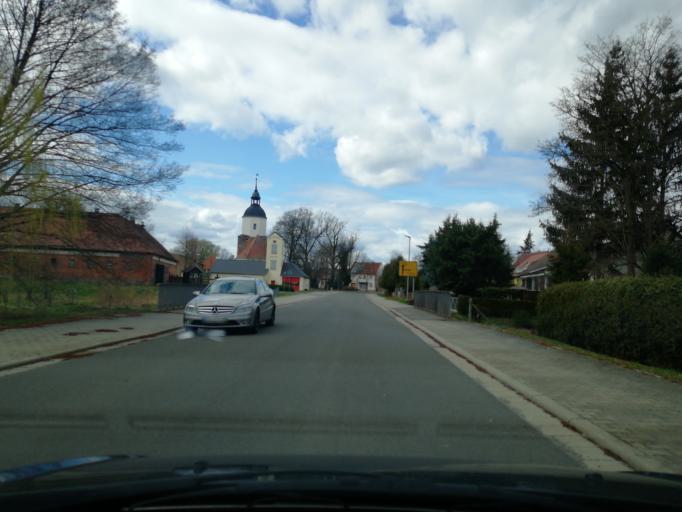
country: DE
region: Brandenburg
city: Altdobern
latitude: 51.7133
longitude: 14.0424
